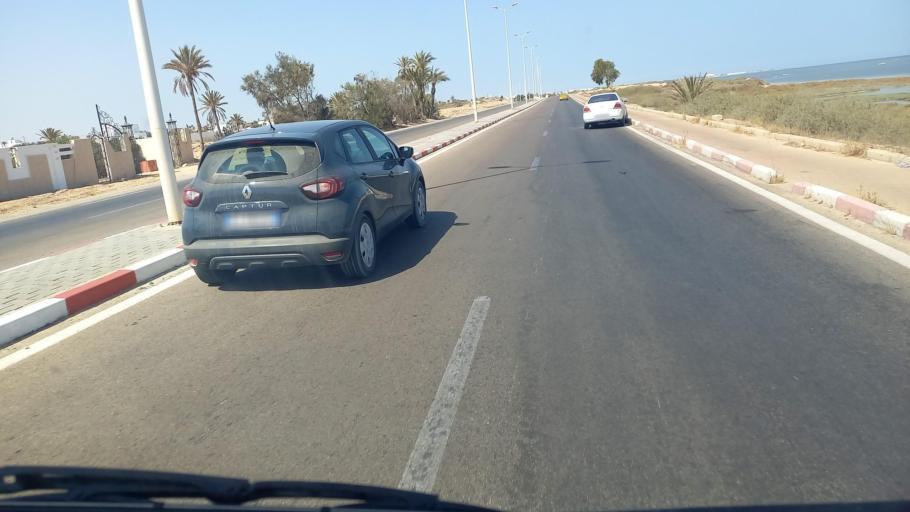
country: TN
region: Madanin
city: Houmt Souk
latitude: 33.8742
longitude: 10.9254
